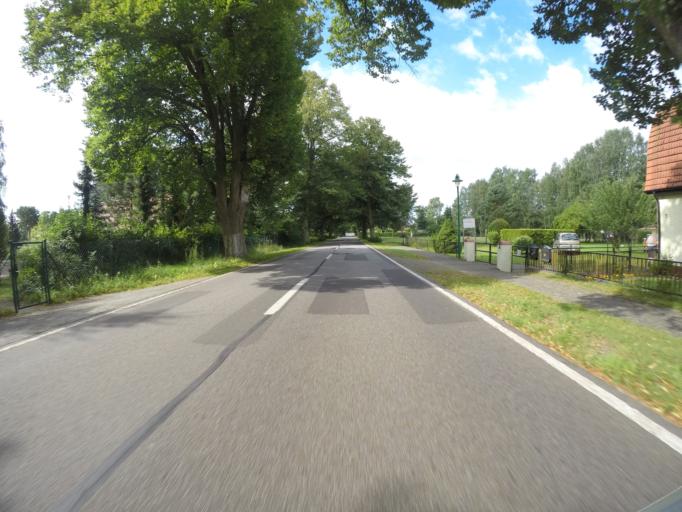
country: DE
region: Mecklenburg-Vorpommern
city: Wesenberg
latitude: 53.2031
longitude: 12.9106
